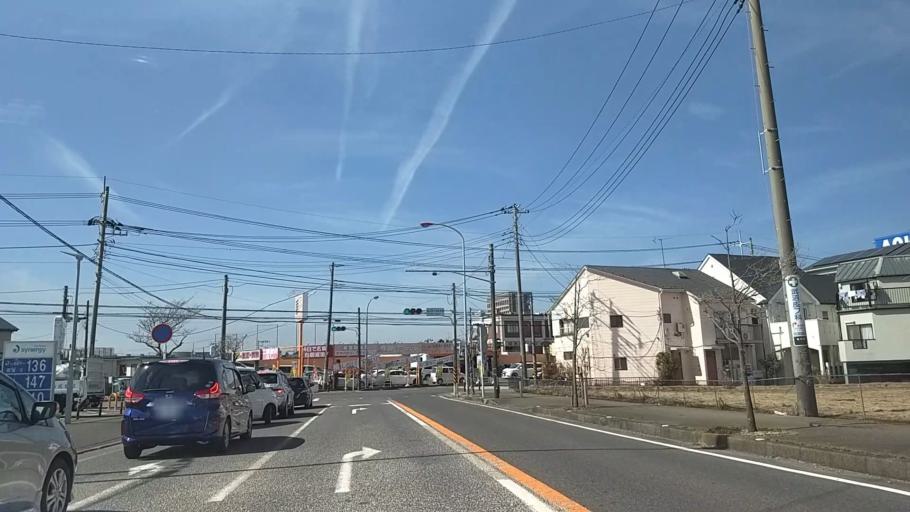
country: JP
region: Kanagawa
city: Fujisawa
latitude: 35.3792
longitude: 139.4770
